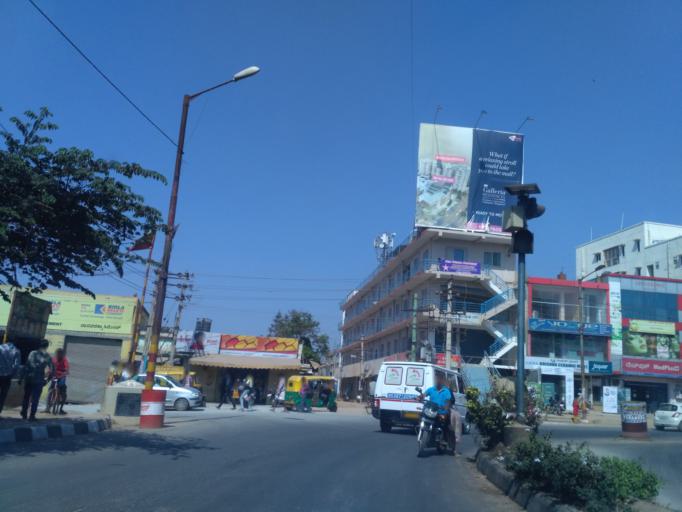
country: IN
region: Karnataka
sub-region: Bangalore Urban
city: Yelahanka
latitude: 13.0976
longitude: 77.5627
